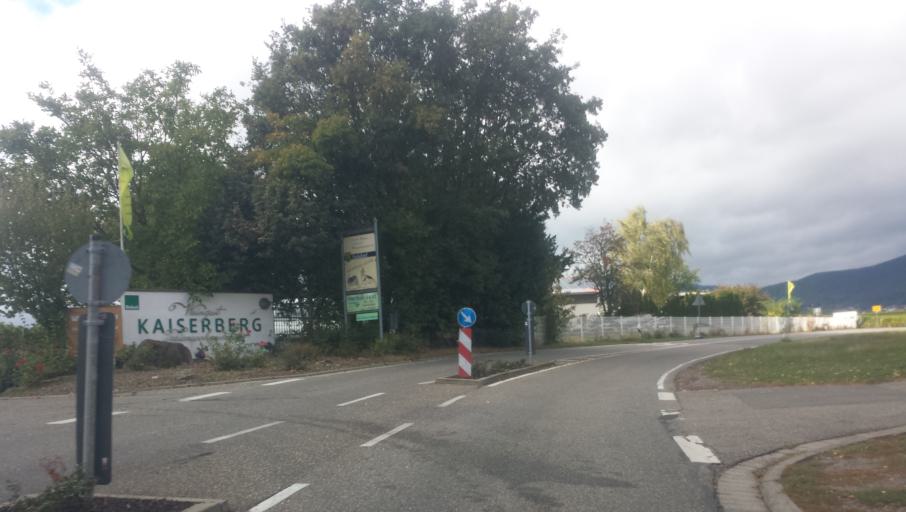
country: DE
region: Rheinland-Pfalz
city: Bochingen
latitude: 49.2225
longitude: 8.1028
